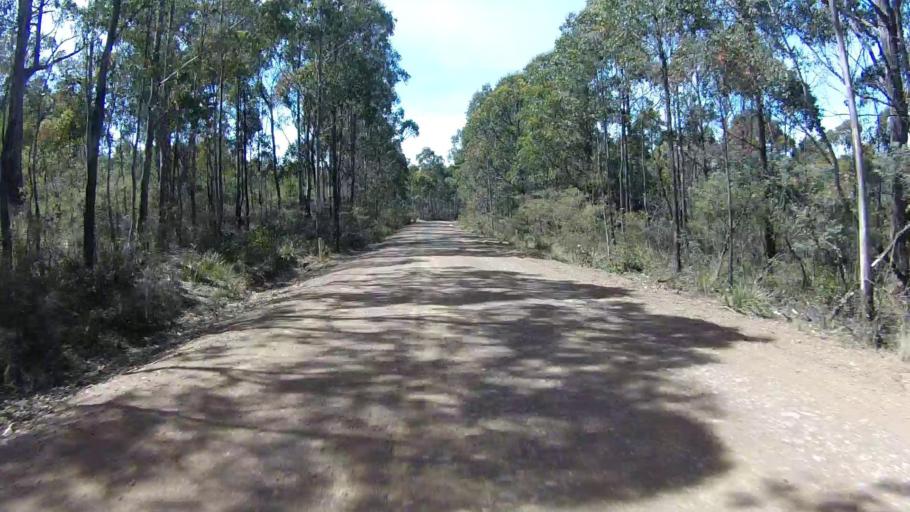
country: AU
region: Tasmania
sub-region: Sorell
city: Sorell
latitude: -42.6740
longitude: 147.7278
